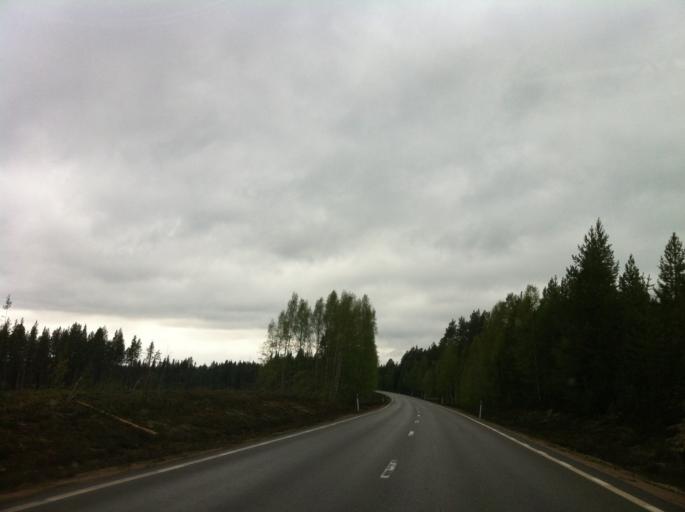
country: SE
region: Jaemtland
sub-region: Harjedalens Kommun
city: Sveg
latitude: 62.1203
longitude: 14.1675
